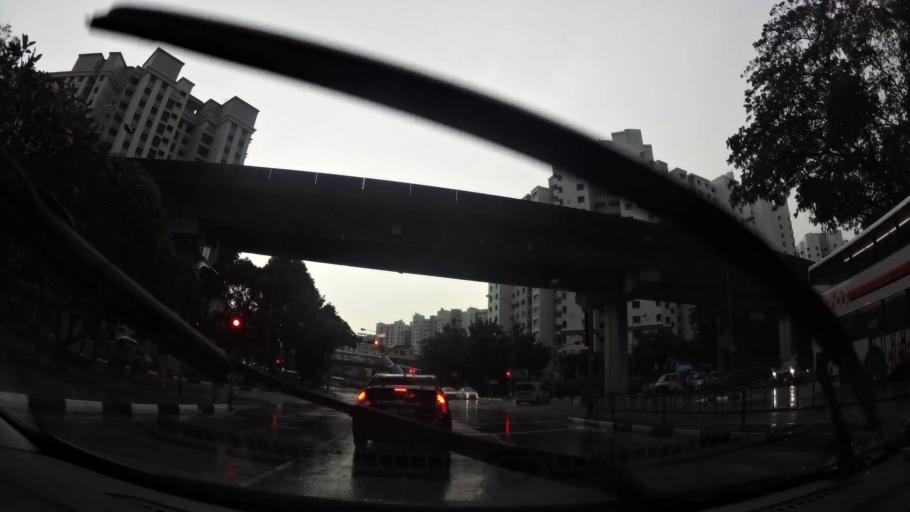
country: MY
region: Johor
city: Kampung Pasir Gudang Baru
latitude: 1.3944
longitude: 103.9016
